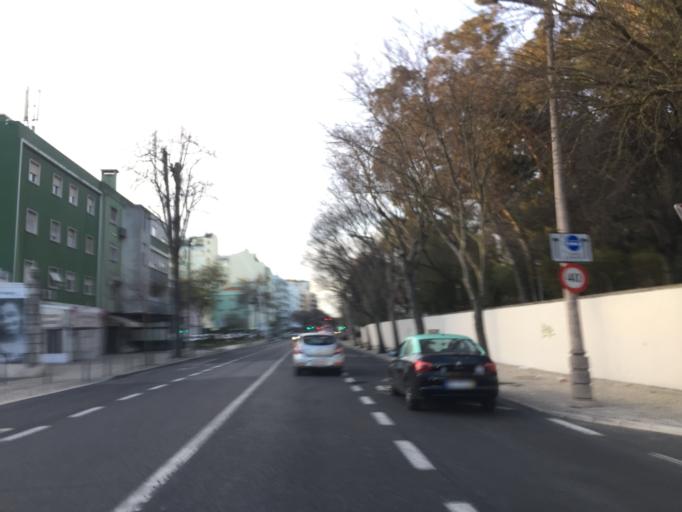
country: PT
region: Lisbon
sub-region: Odivelas
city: Olival do Basto
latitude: 38.7688
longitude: -9.1587
